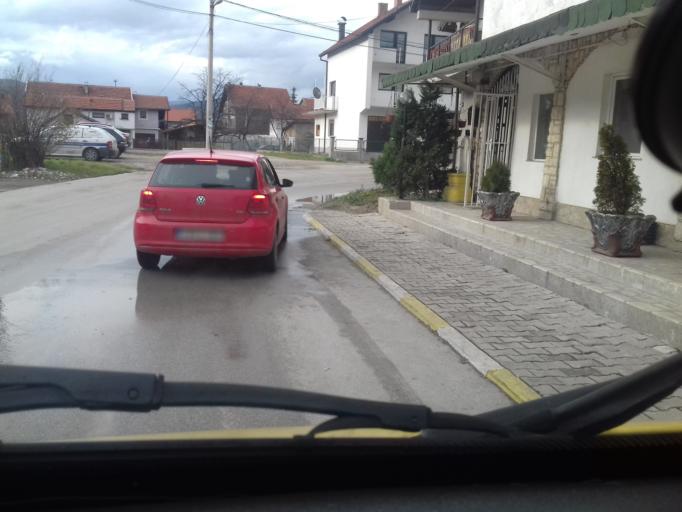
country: BA
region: Federation of Bosnia and Herzegovina
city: Zenica
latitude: 44.1894
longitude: 17.9459
